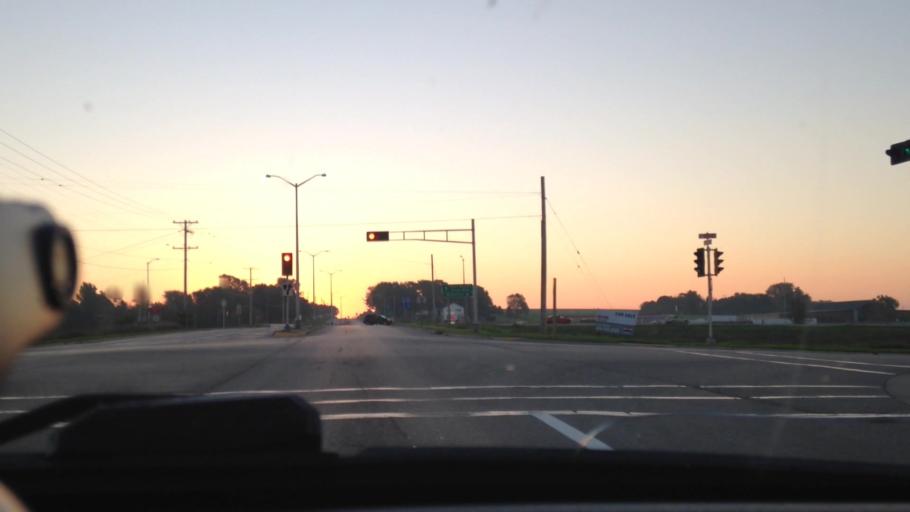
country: US
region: Wisconsin
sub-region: Dodge County
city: Lomira
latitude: 43.5871
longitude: -88.4336
